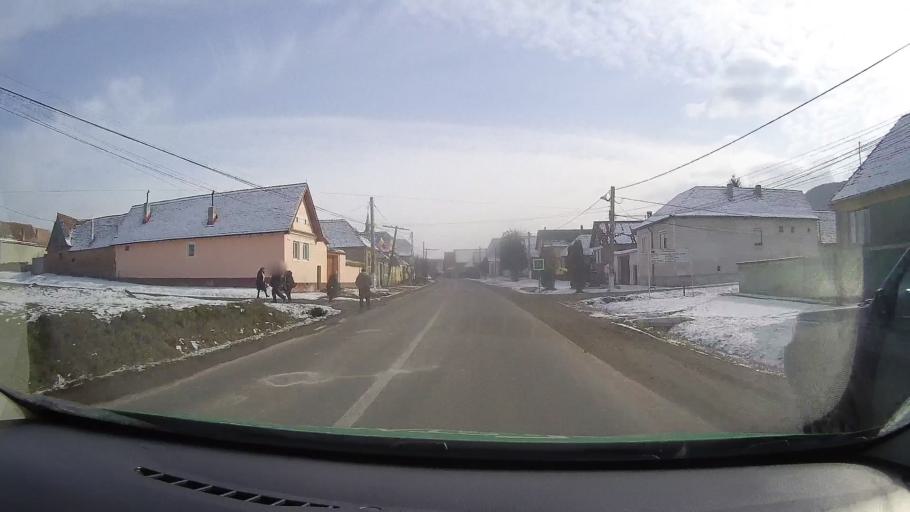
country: RO
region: Mures
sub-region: Comuna Apold
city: Saes
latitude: 46.1581
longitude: 24.7664
